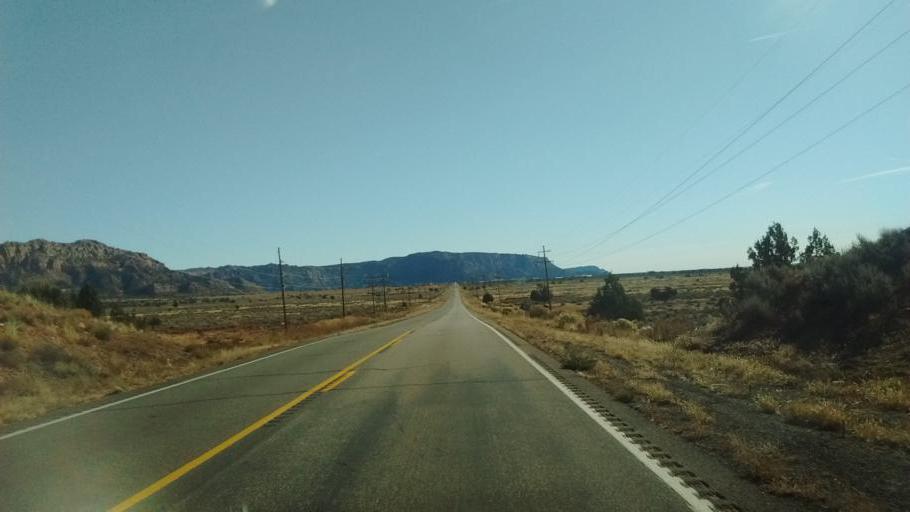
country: US
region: Arizona
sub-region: Mohave County
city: Colorado City
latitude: 37.0195
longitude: -113.0339
